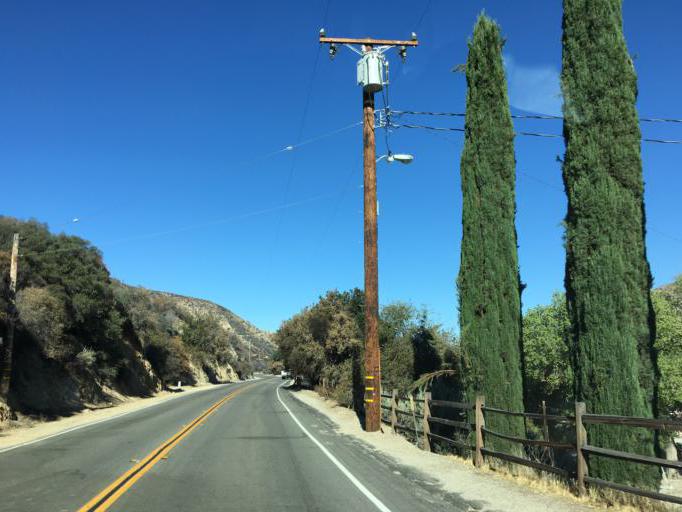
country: US
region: California
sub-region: Los Angeles County
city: Acton
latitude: 34.4375
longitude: -118.2676
